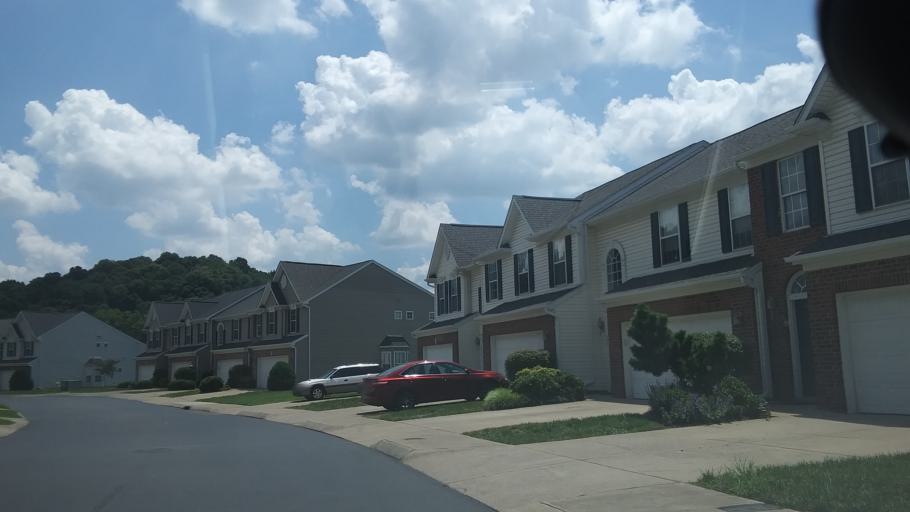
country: US
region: Tennessee
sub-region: Davidson County
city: Belle Meade
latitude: 36.1185
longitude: -86.9168
